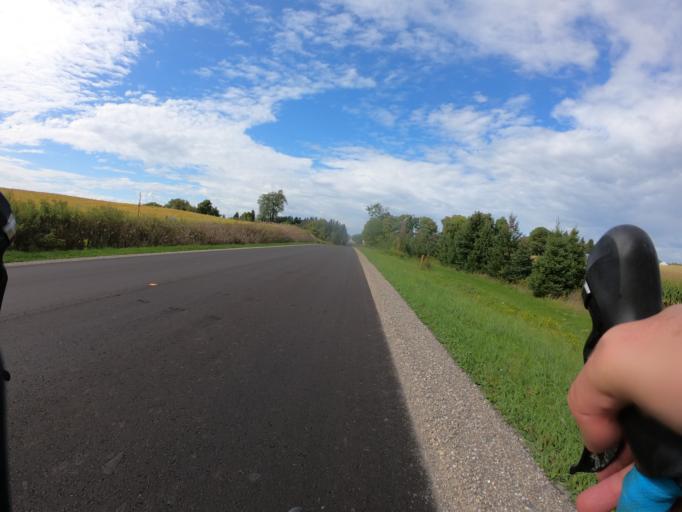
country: CA
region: Ontario
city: Kitchener
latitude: 43.3818
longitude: -80.6232
